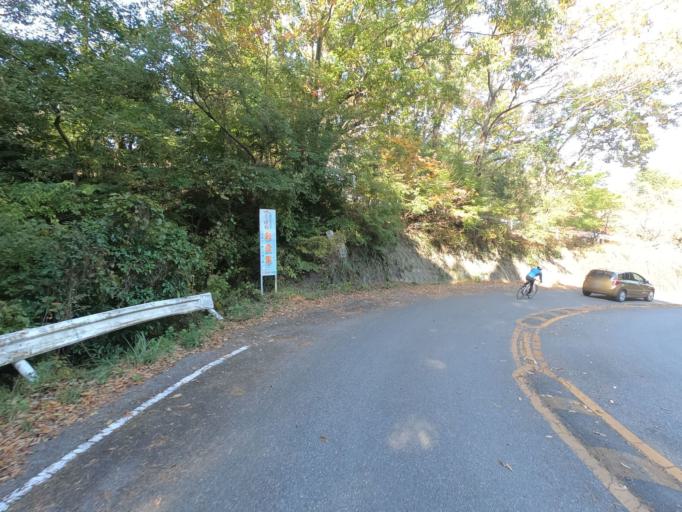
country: JP
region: Ibaraki
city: Tsukuba
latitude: 36.2331
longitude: 140.1273
